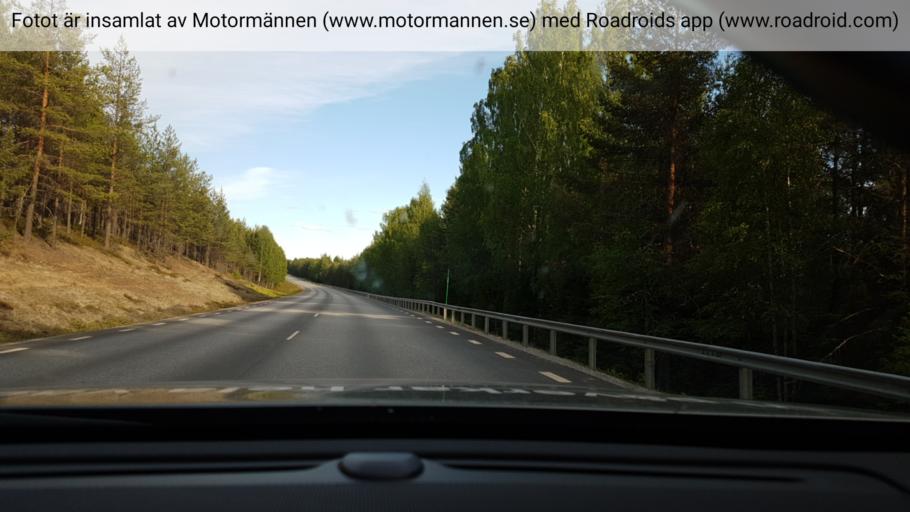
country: SE
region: Vaesterbotten
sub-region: Vindelns Kommun
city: Vindeln
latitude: 64.1511
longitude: 19.8582
